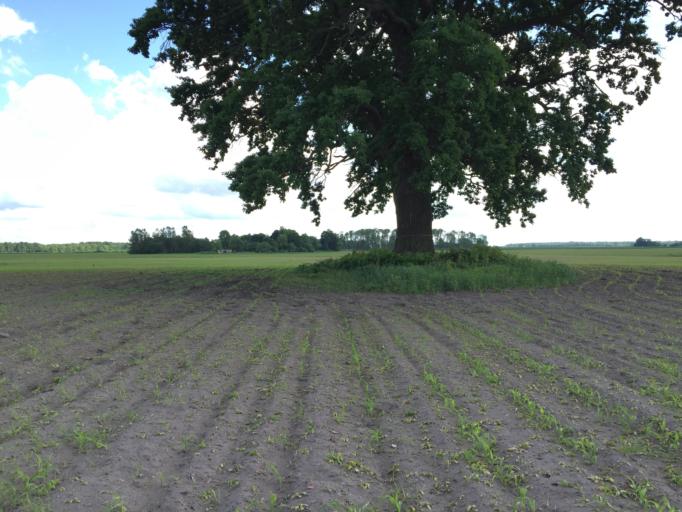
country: LV
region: Dobeles Rajons
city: Dobele
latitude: 56.6739
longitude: 23.3938
